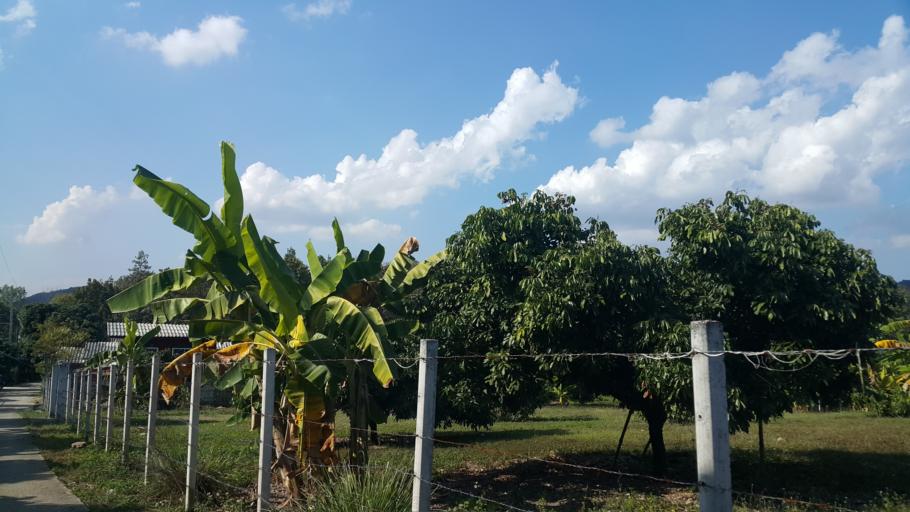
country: TH
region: Lamphun
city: Ban Thi
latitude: 18.5886
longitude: 99.1591
